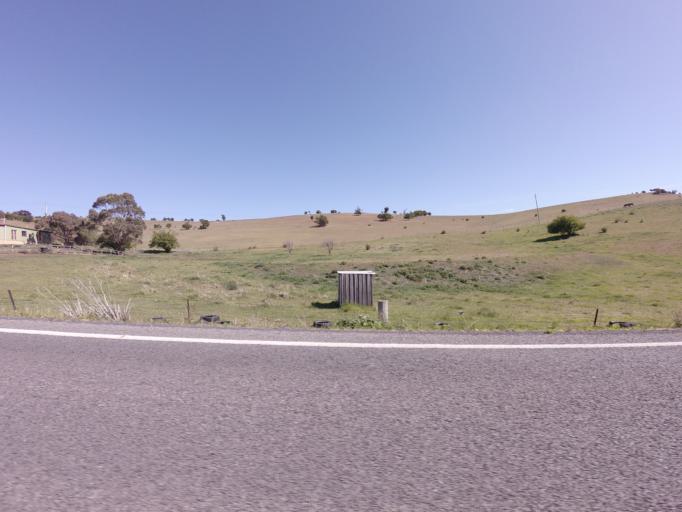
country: AU
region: Tasmania
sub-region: Derwent Valley
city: New Norfolk
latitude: -42.5574
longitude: 146.8687
